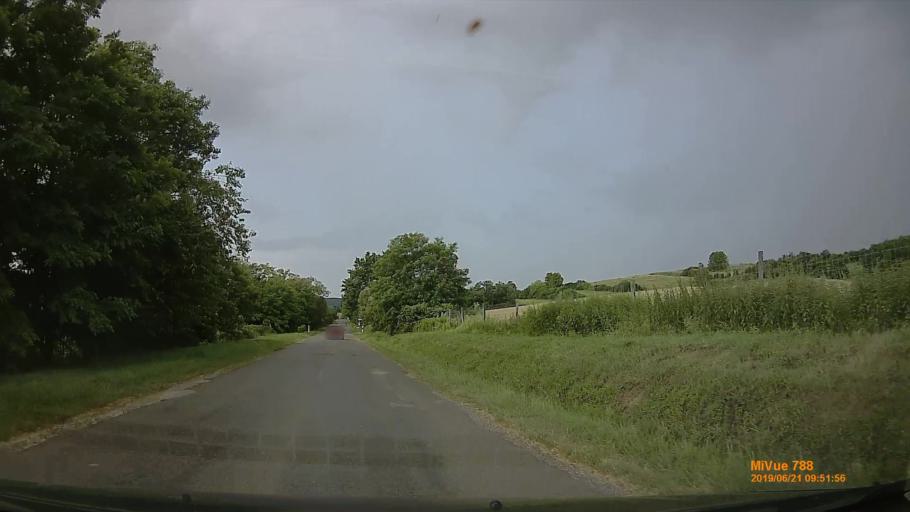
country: HU
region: Baranya
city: Sasd
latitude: 46.2472
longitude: 18.0192
